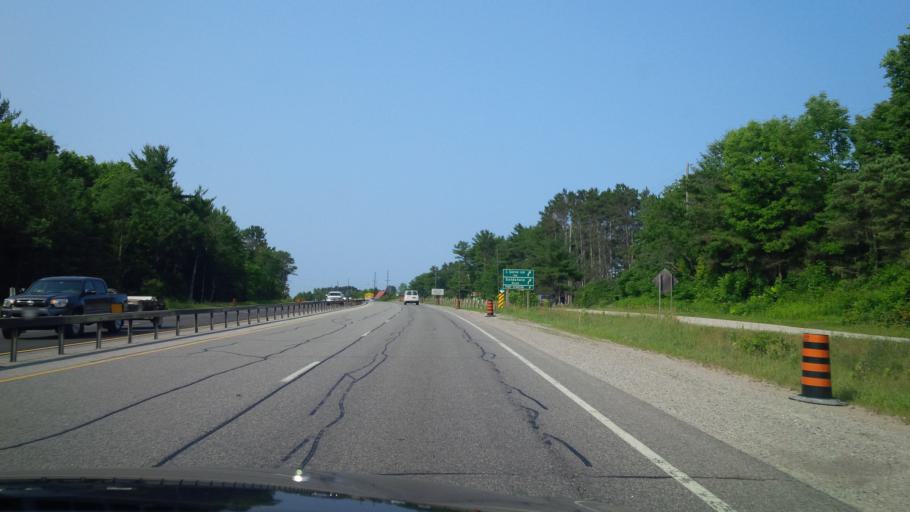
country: CA
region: Ontario
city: Orillia
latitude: 44.7276
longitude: -79.3708
